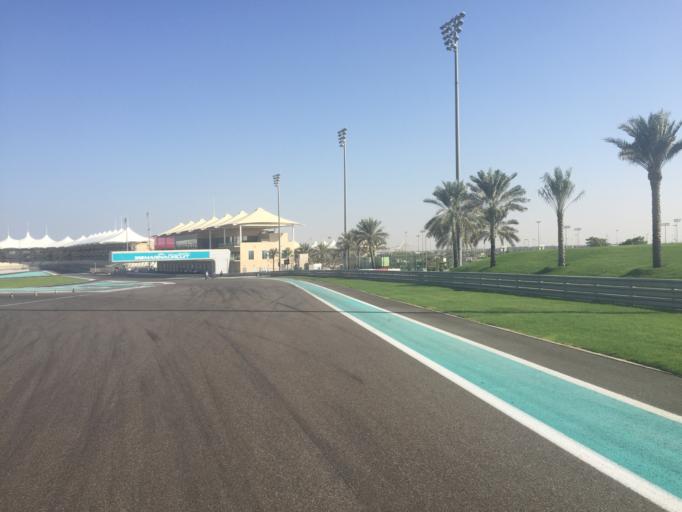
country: AE
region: Abu Dhabi
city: Abu Dhabi
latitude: 24.4742
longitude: 54.6058
